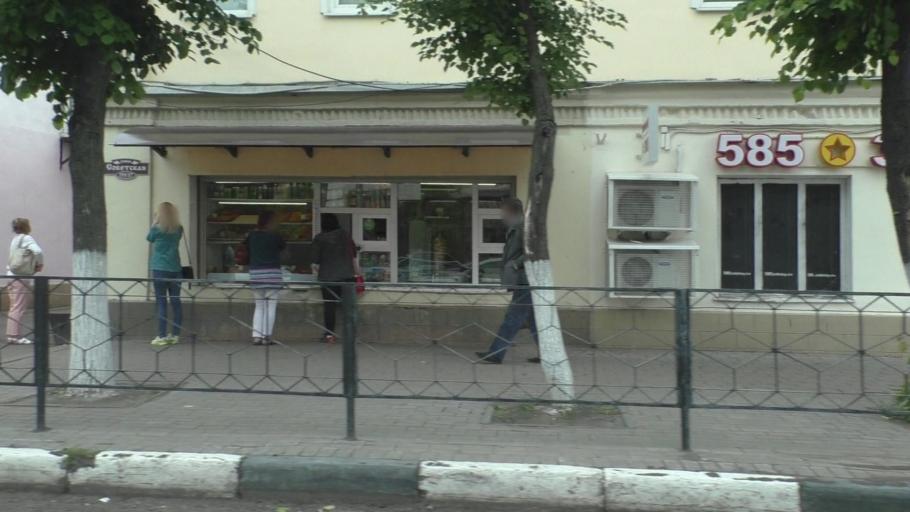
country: RU
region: Moskovskaya
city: Yegor'yevsk
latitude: 55.3781
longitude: 39.0434
